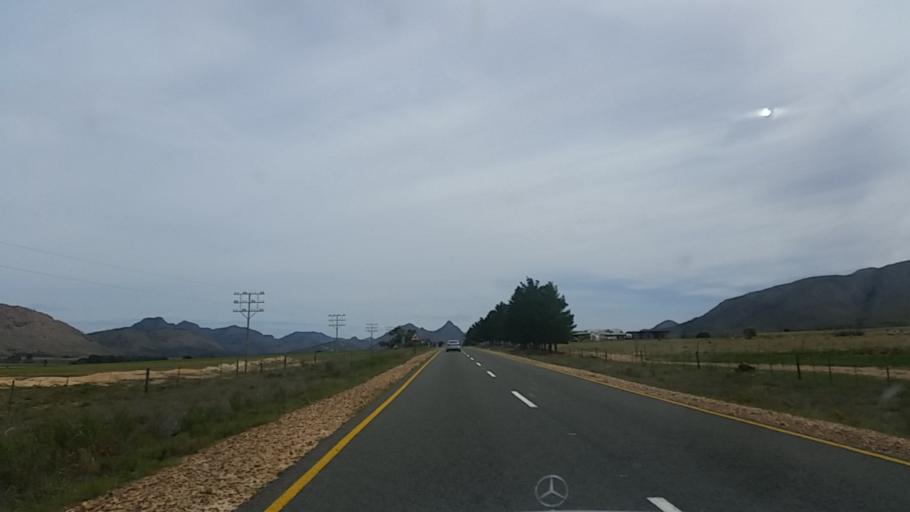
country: ZA
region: Western Cape
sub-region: Eden District Municipality
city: George
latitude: -33.8165
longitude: 22.5131
